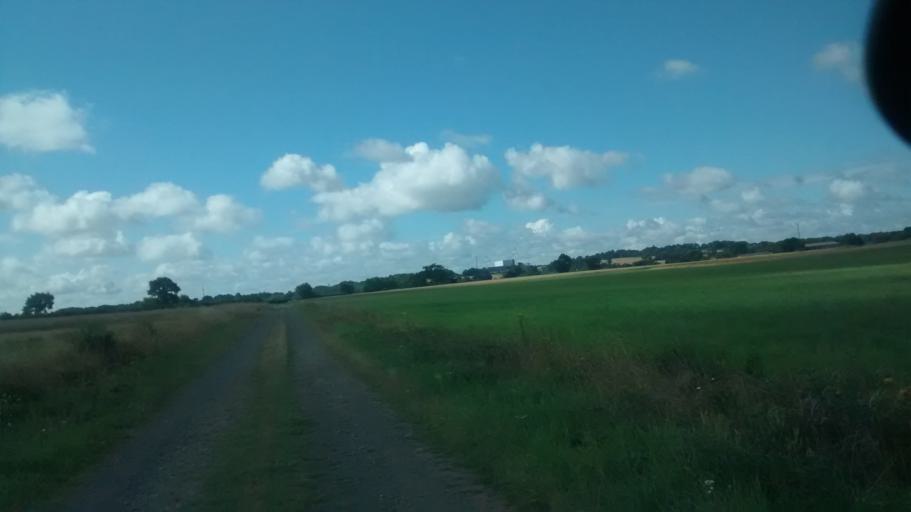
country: FR
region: Brittany
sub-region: Departement d'Ille-et-Vilaine
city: La Dominelais
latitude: 47.7712
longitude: -1.7153
